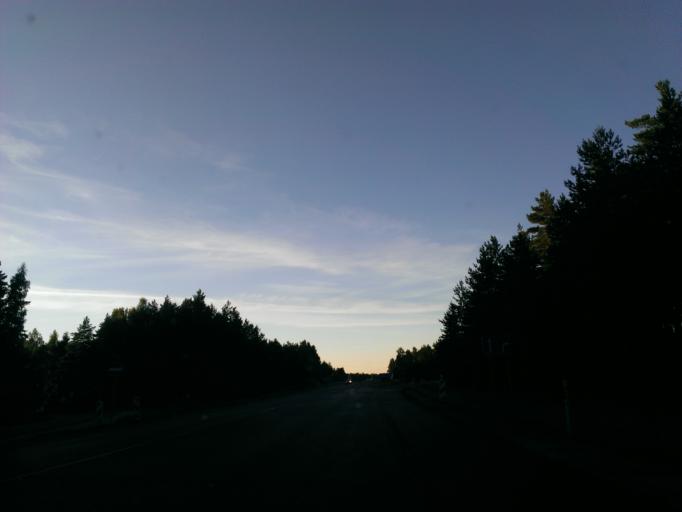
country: LV
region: Riga
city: Bergi
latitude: 57.0062
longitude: 24.3075
